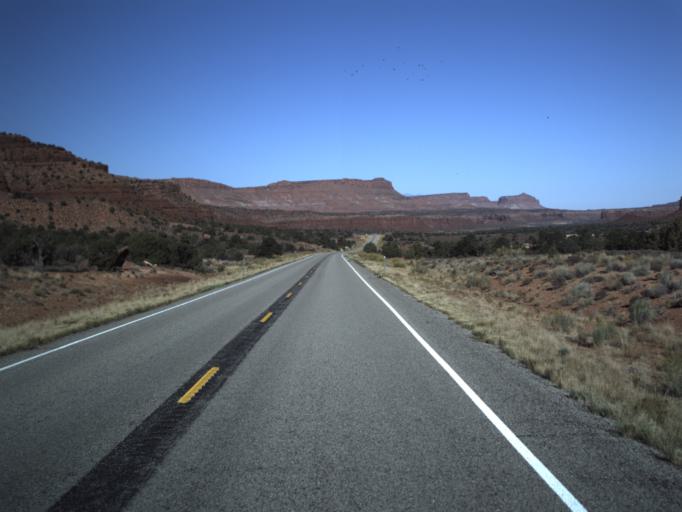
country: US
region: Utah
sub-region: San Juan County
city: Blanding
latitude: 37.6651
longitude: -110.1930
